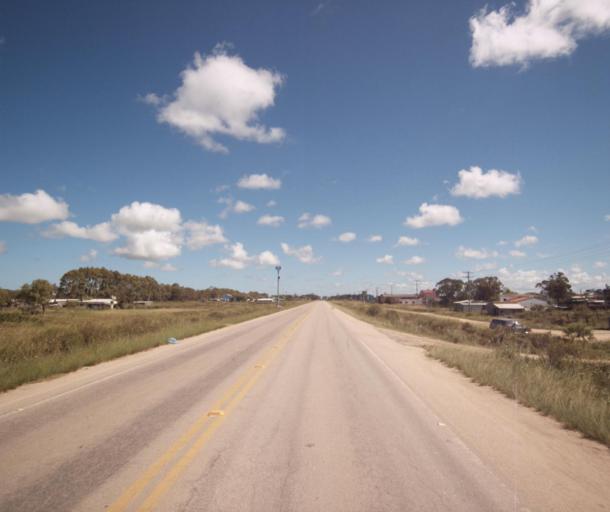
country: BR
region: Rio Grande do Sul
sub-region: Santa Vitoria Do Palmar
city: Santa Vitoria do Palmar
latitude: -33.5270
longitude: -53.3419
